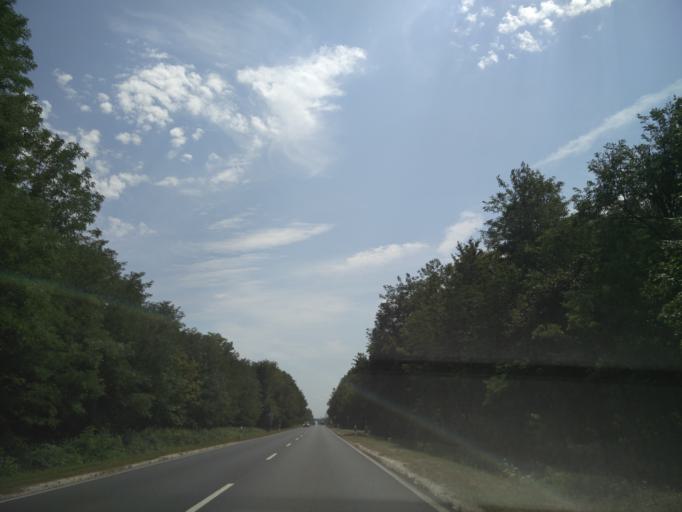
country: HU
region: Zala
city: Zalaegerszeg
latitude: 46.8713
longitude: 16.8535
